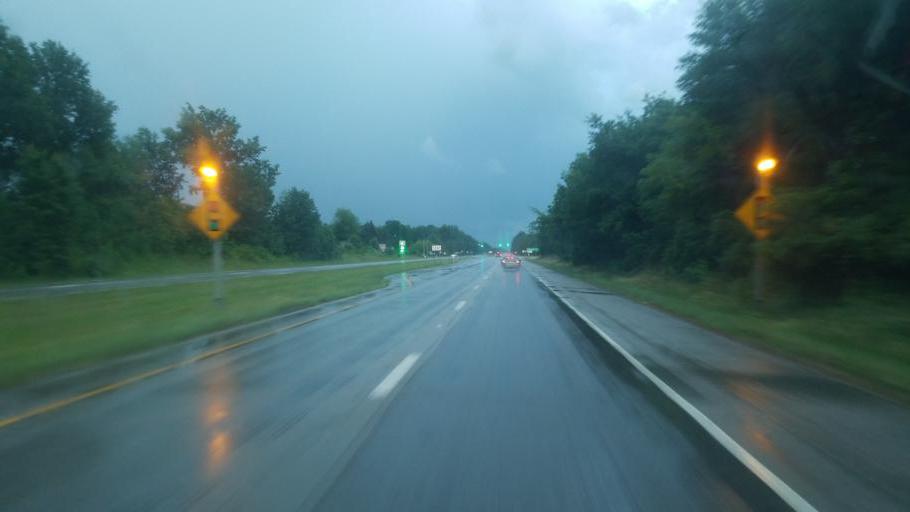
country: US
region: Ohio
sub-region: Wayne County
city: Doylestown
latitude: 40.9633
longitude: -81.6600
